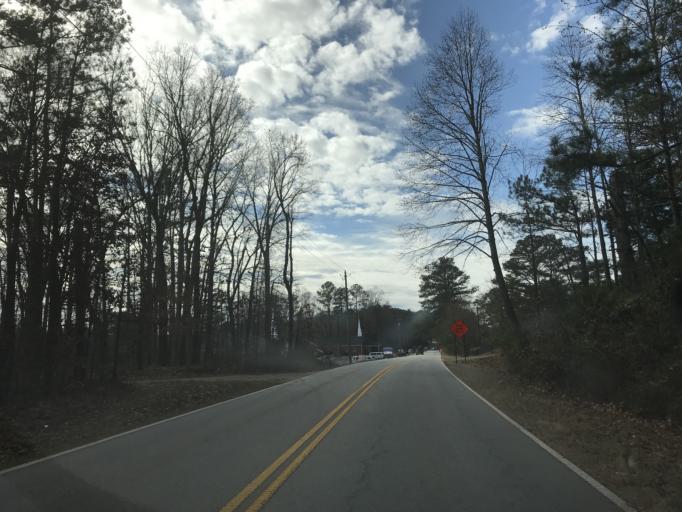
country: US
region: Georgia
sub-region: Douglas County
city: Douglasville
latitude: 33.7827
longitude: -84.7886
